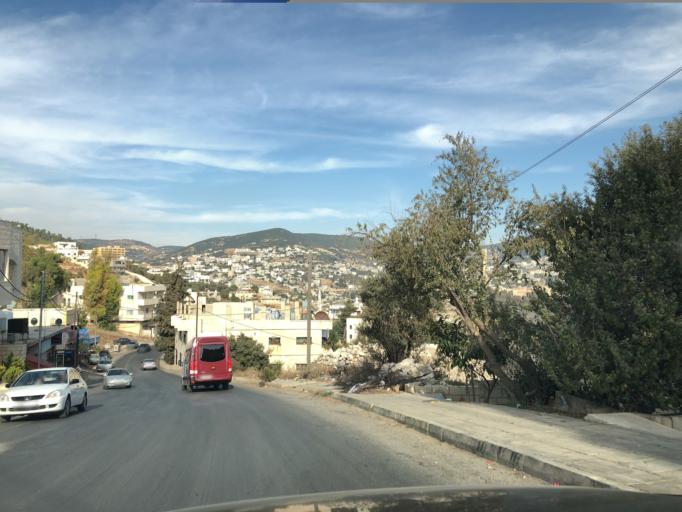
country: JO
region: Ajlun
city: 'Ajlun
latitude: 32.3298
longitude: 35.7392
